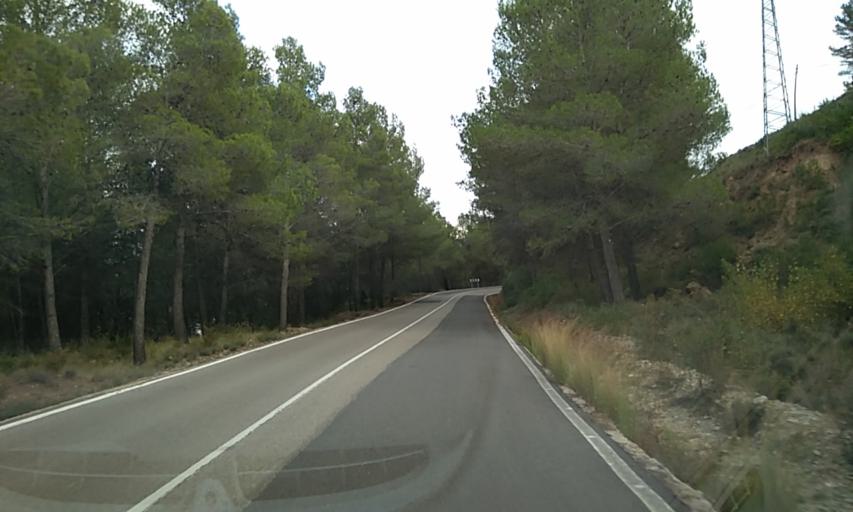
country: ES
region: Valencia
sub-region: Provincia de Castello
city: Puebla de Arenoso
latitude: 40.0884
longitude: -0.5617
